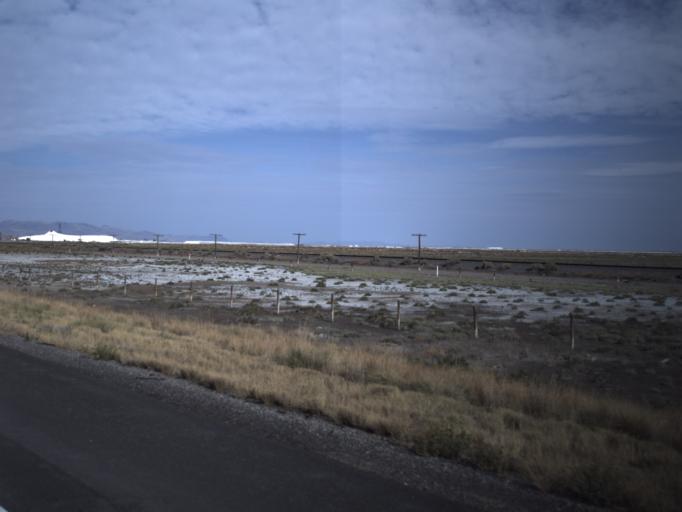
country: US
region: Utah
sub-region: Tooele County
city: Grantsville
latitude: 40.7017
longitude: -112.4917
